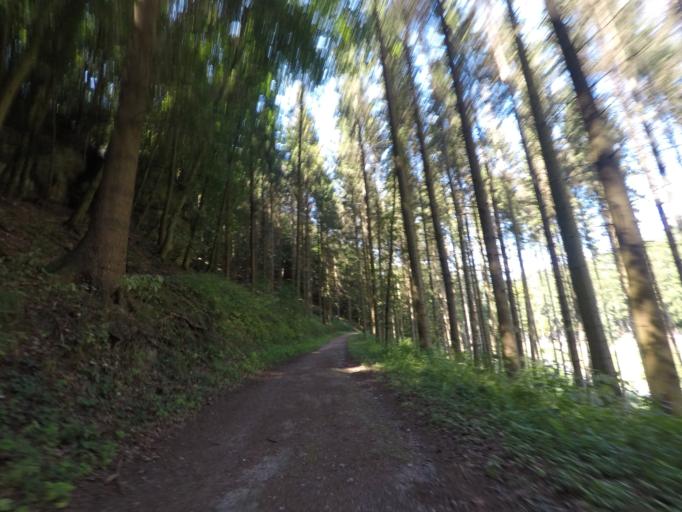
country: LU
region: Luxembourg
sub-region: Canton de Luxembourg
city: Strassen
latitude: 49.6271
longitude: 6.0969
